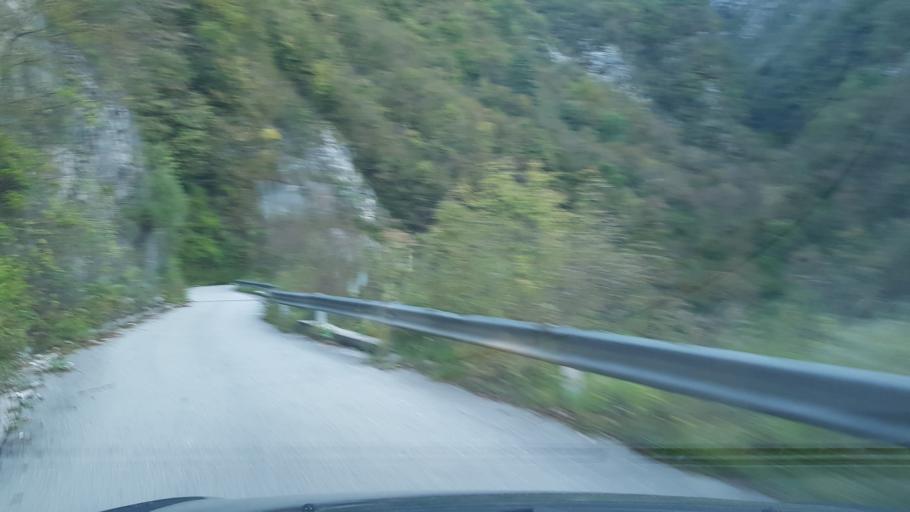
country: IT
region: Friuli Venezia Giulia
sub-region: Provincia di Udine
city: Venzone
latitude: 46.3346
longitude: 13.1806
